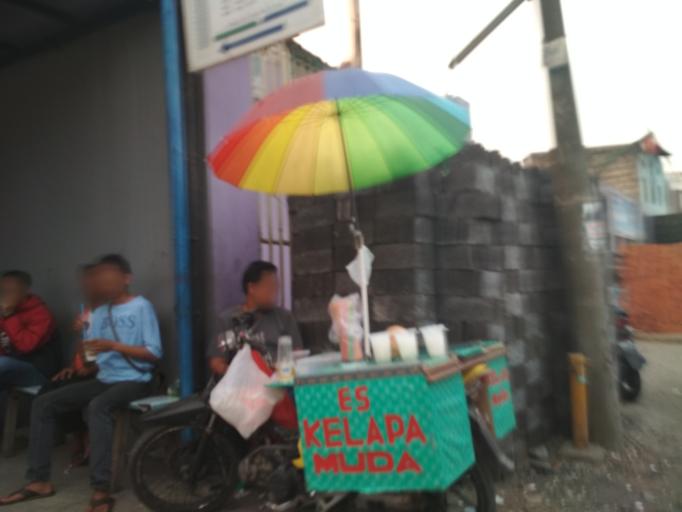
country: ID
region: West Java
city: Caringin
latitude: -6.6614
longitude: 106.8448
